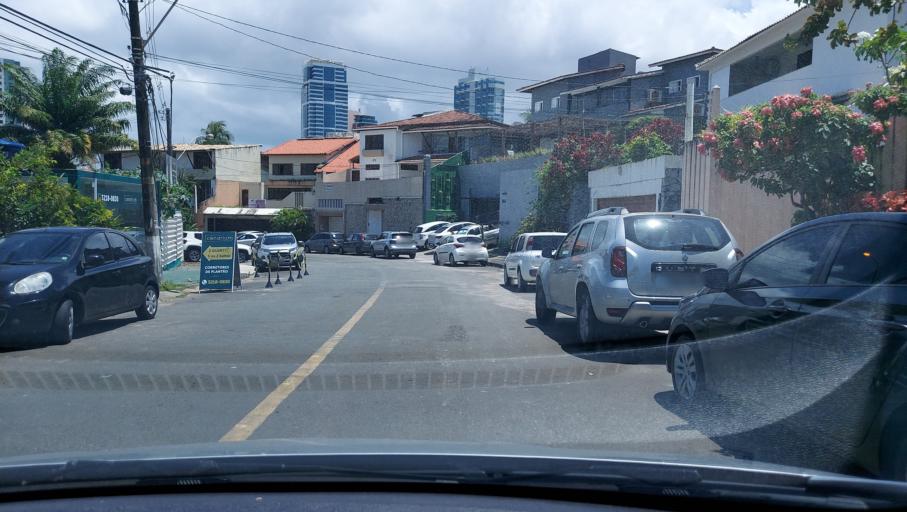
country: BR
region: Bahia
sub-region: Salvador
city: Salvador
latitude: -12.9823
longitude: -38.4570
